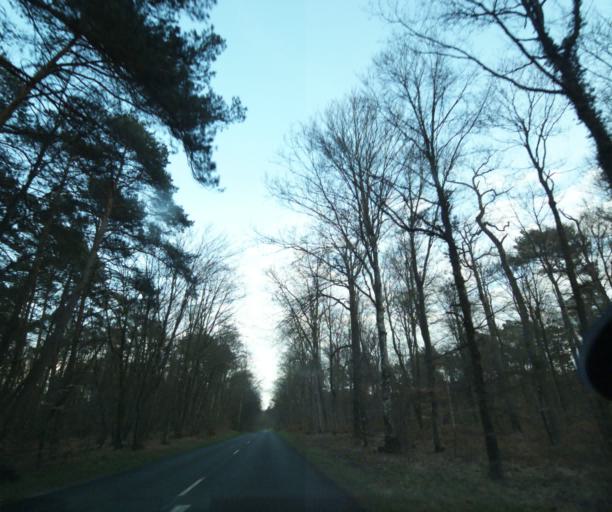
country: FR
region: Ile-de-France
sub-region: Departement de Seine-et-Marne
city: Avon
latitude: 48.3751
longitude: 2.7434
